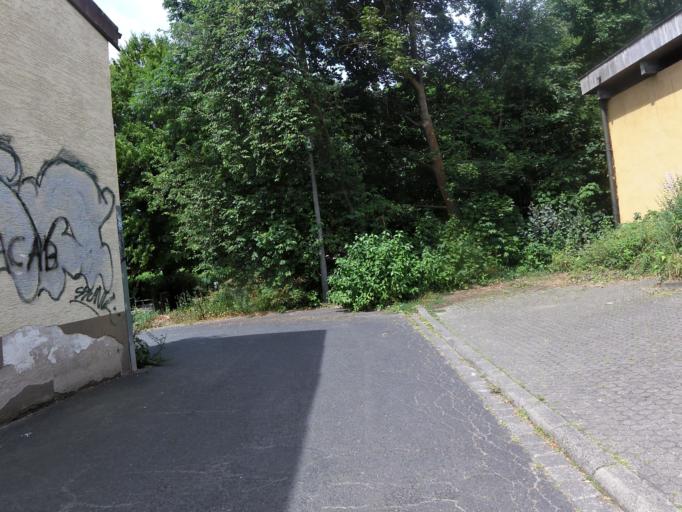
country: DE
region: Bavaria
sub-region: Regierungsbezirk Unterfranken
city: Estenfeld
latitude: 49.8093
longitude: 9.9853
